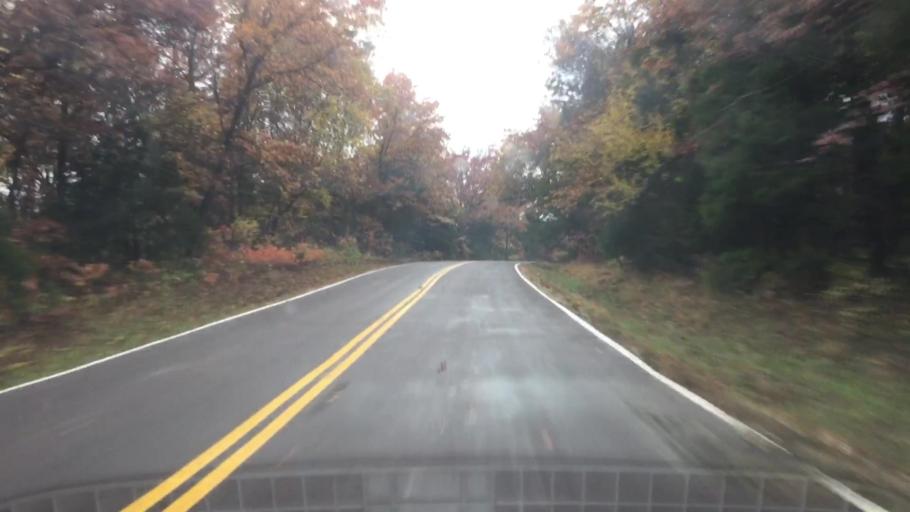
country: US
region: Missouri
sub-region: Boone County
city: Columbia
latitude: 38.8706
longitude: -92.3213
